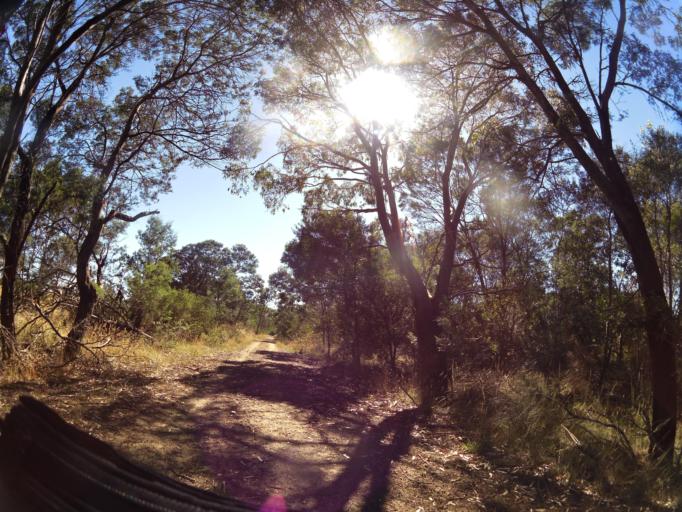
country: AU
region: Victoria
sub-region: Ballarat North
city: Delacombe
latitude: -37.6702
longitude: 143.4552
